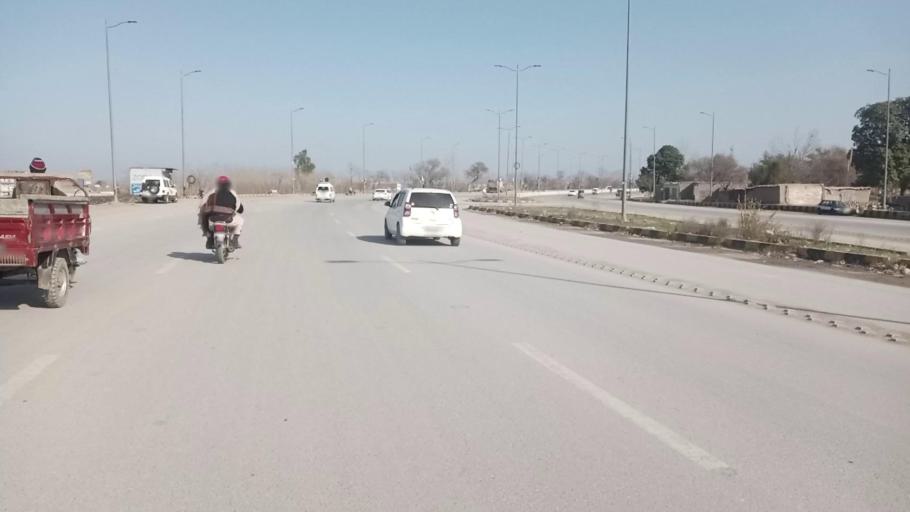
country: PK
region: Khyber Pakhtunkhwa
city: Peshawar
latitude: 34.0396
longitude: 71.5356
